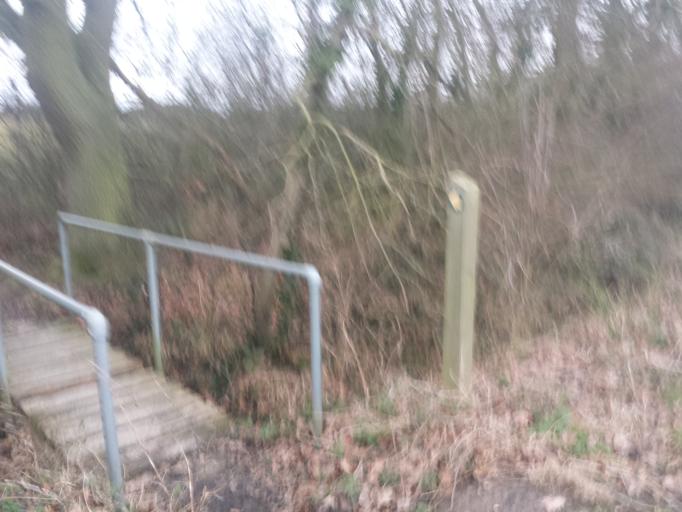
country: GB
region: England
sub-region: Essex
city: Little Clacton
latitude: 51.8456
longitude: 1.1475
